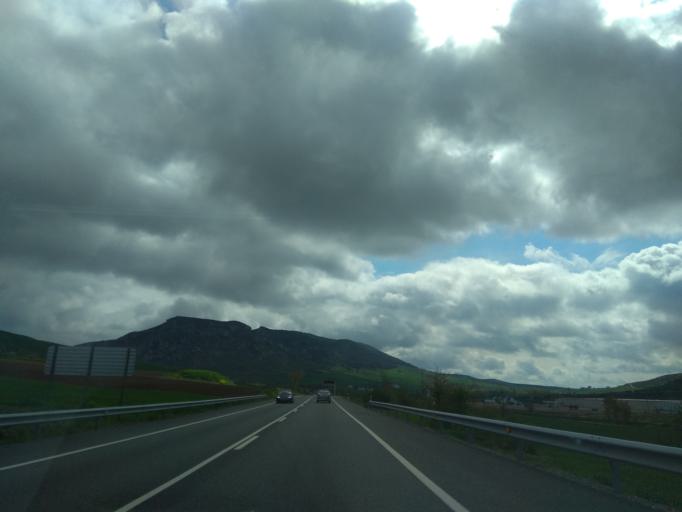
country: ES
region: Castille and Leon
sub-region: Provincia de Burgos
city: Pancorbo
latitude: 42.6291
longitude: -3.1296
